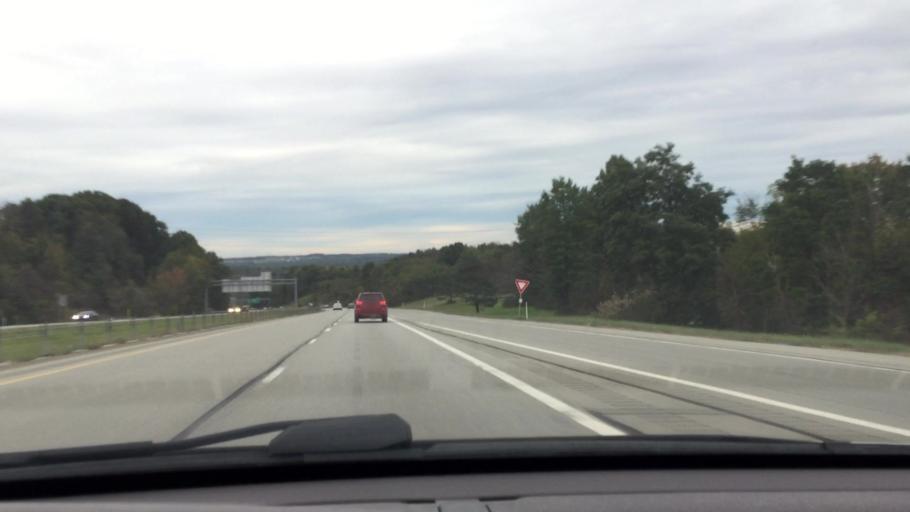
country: US
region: Pennsylvania
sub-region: Lawrence County
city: Oakwood
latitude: 41.0146
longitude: -80.3901
